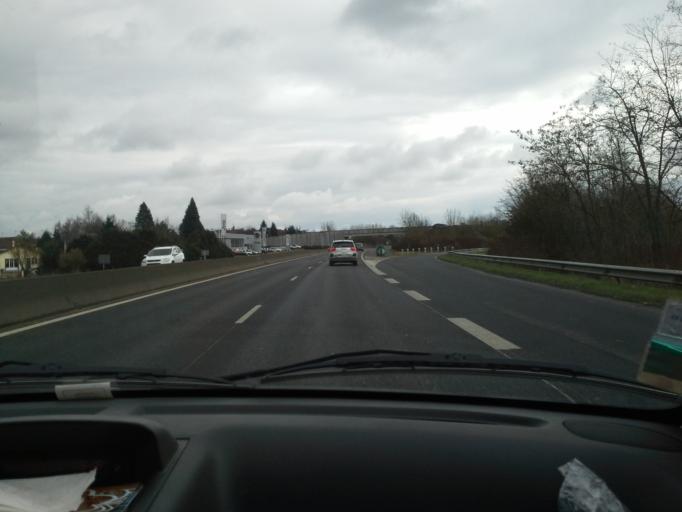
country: FR
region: Centre
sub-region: Departement du Loir-et-Cher
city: Vineuil
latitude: 47.5849
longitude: 1.3648
